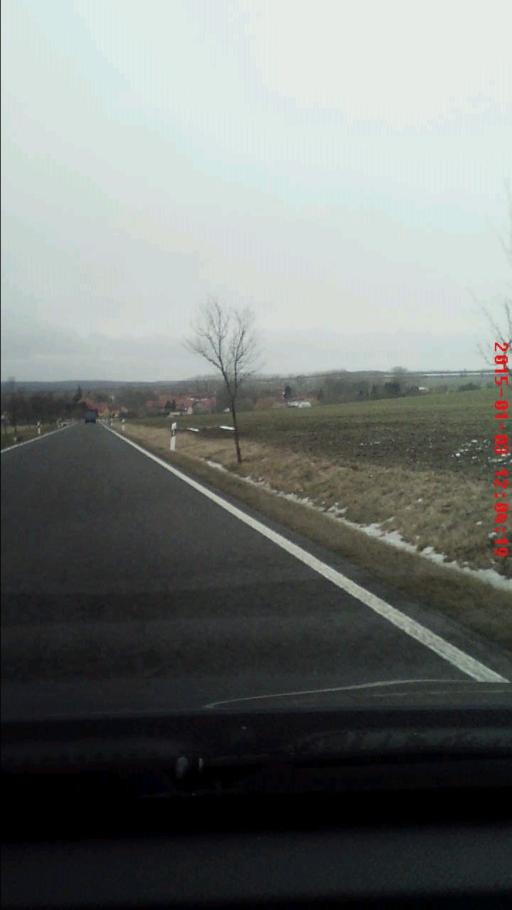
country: DE
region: Thuringia
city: Milda
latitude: 50.8450
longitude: 11.4293
